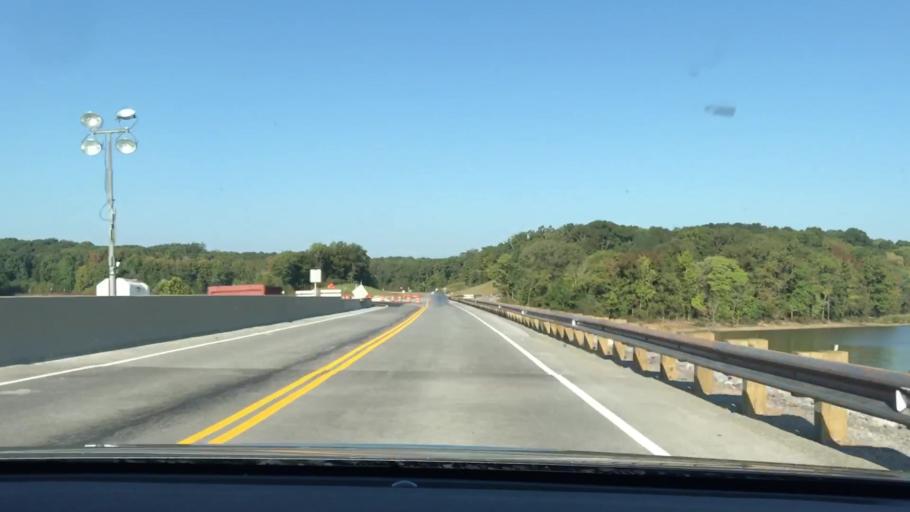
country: US
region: Kentucky
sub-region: Trigg County
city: Cadiz
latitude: 36.8018
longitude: -87.9829
